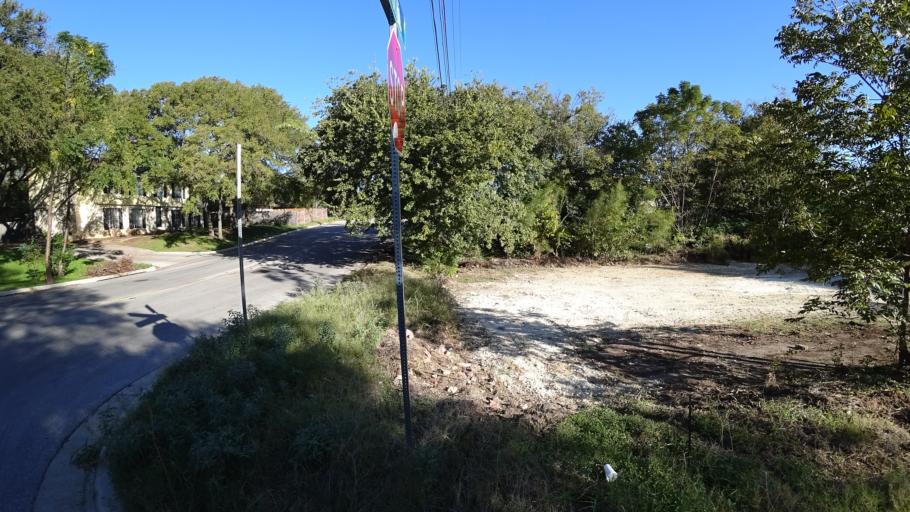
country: US
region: Texas
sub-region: Travis County
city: Austin
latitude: 30.3073
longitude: -97.6762
